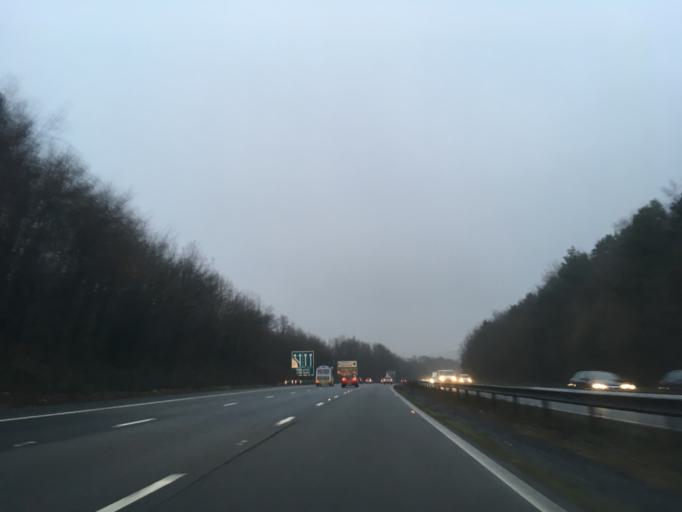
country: GB
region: Wales
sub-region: Cardiff
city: Radyr
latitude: 51.5208
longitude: -3.2717
